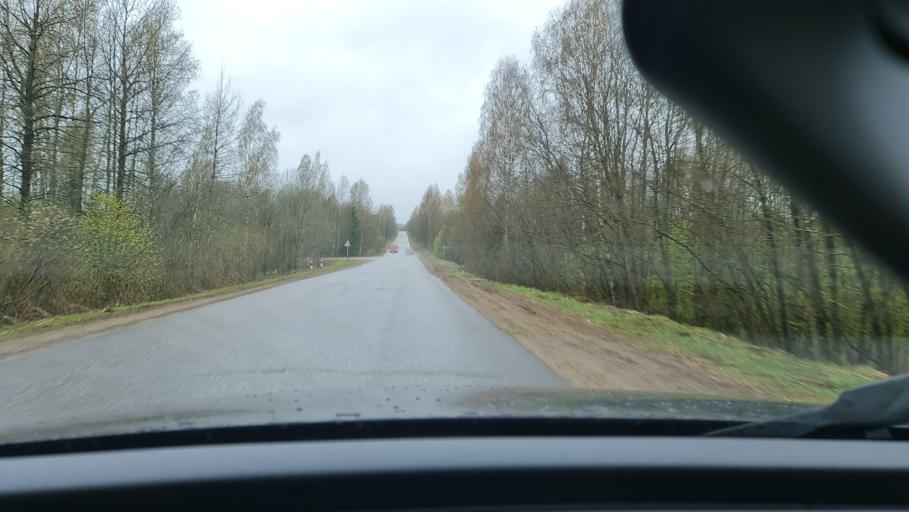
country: RU
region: Novgorod
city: Kresttsy
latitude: 57.9732
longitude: 32.7272
